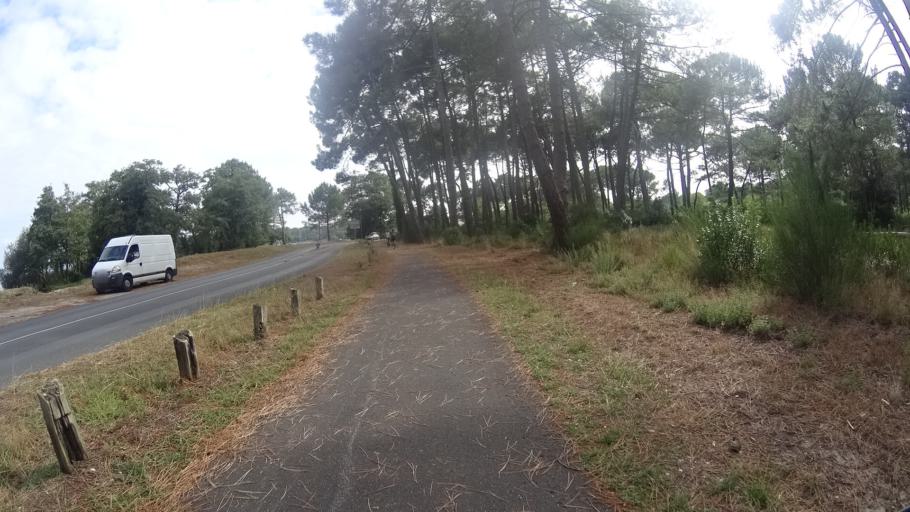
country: FR
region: Aquitaine
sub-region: Departement de la Gironde
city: Lacanau
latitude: 44.9976
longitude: -1.1421
